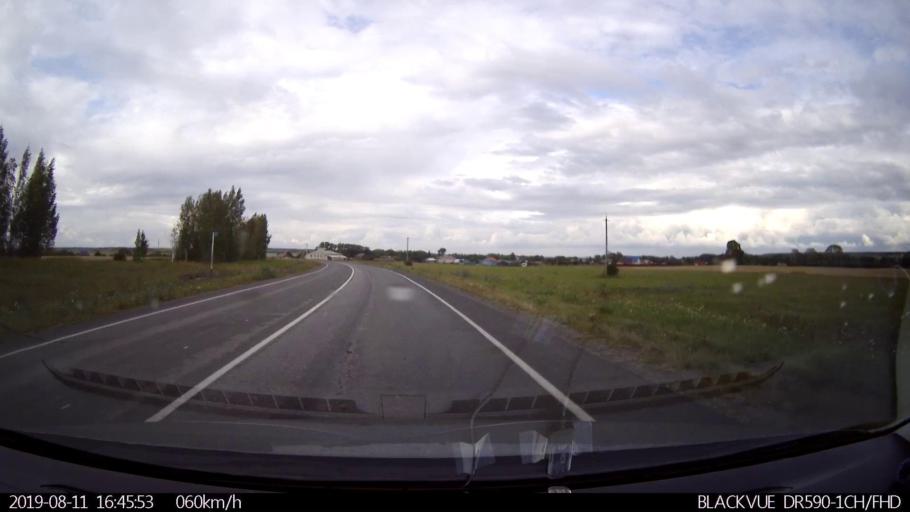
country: RU
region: Ulyanovsk
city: Mayna
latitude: 54.1941
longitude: 47.6885
